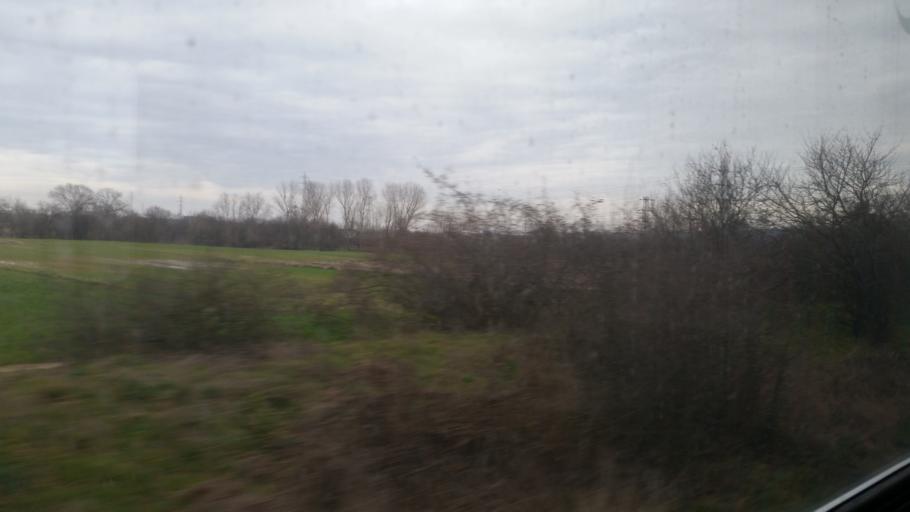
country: TR
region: Tekirdag
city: Velimese
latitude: 41.2578
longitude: 27.9091
